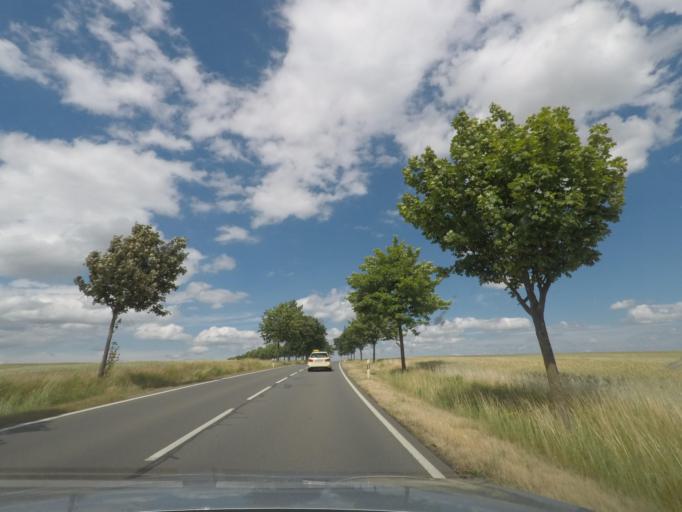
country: DE
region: Saxony-Anhalt
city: Gross Quenstedt
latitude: 51.9382
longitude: 11.1206
